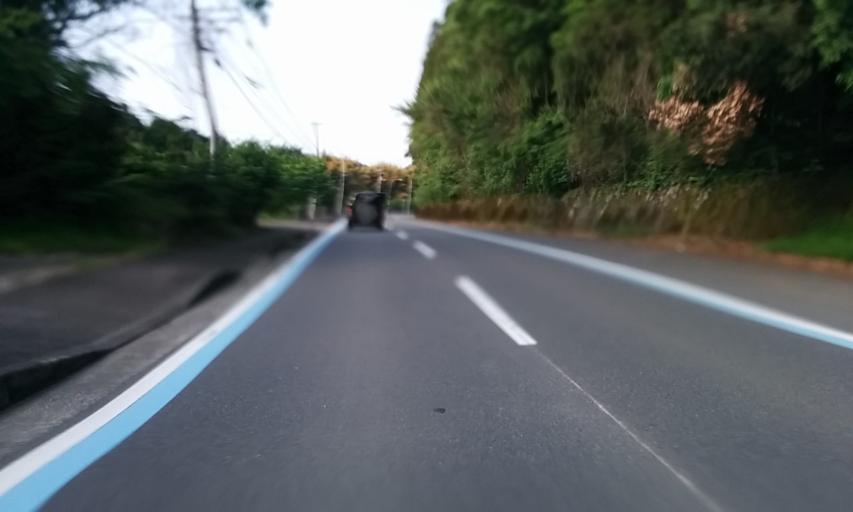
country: JP
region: Ehime
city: Saijo
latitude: 33.8805
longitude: 133.1775
